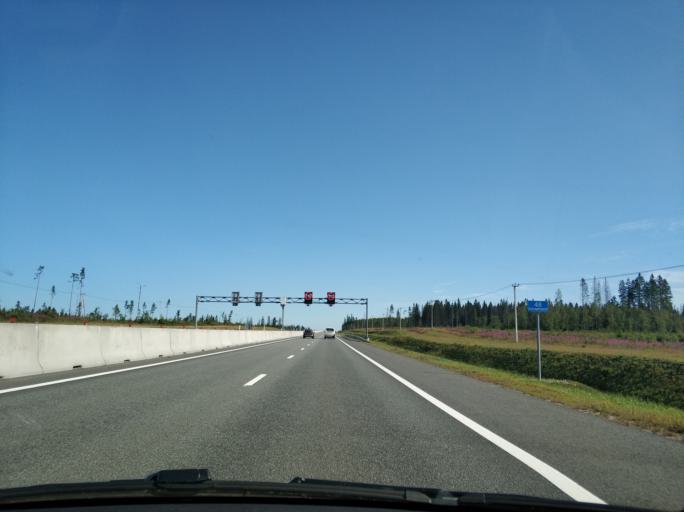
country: RU
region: Leningrad
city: Sosnovo
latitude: 60.4796
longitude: 30.1959
